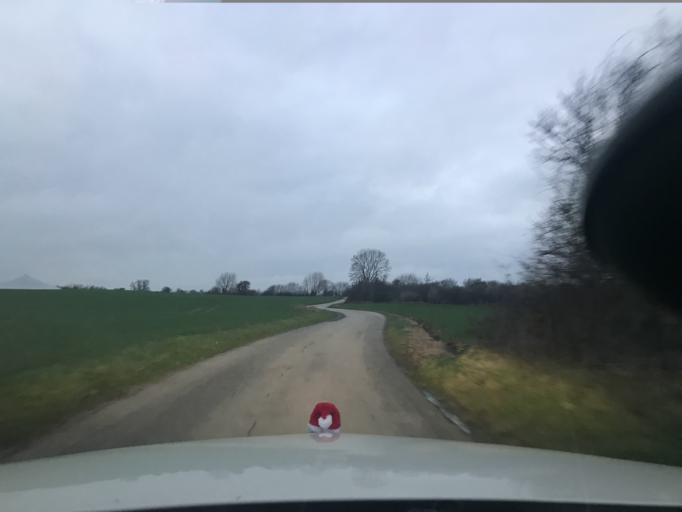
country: DK
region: South Denmark
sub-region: Sonderborg Kommune
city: Dybbol
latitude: 54.8519
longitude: 9.7349
